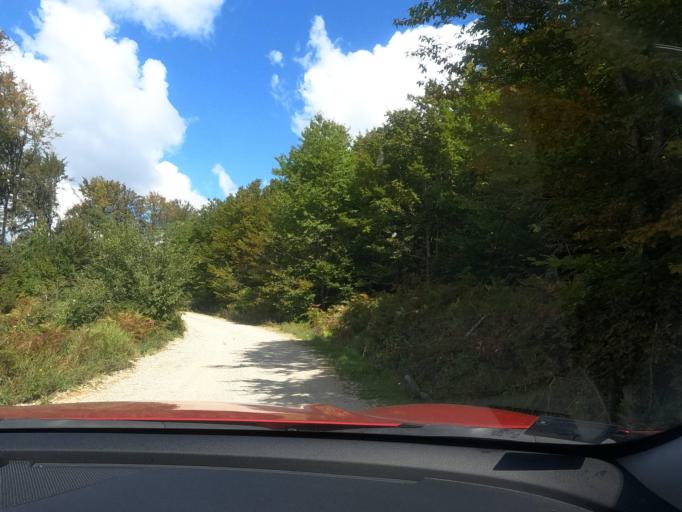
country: HR
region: Karlovacka
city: Vojnic
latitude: 45.2815
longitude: 15.7816
